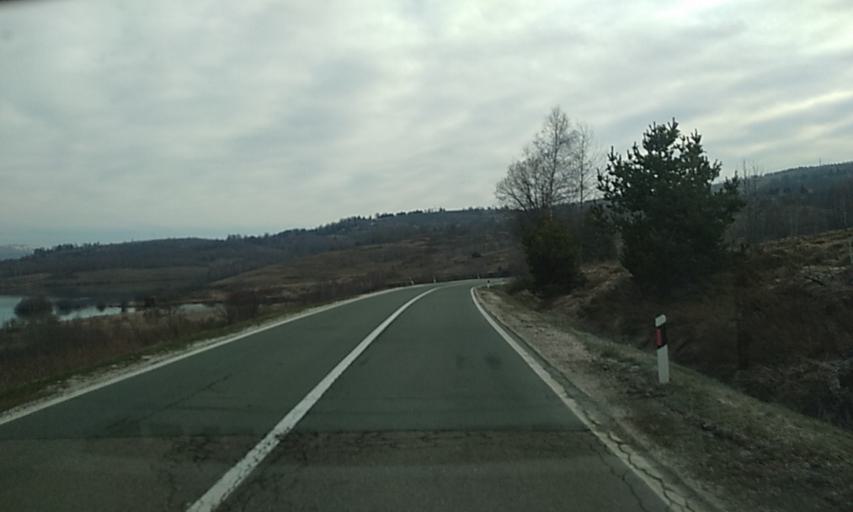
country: RS
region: Central Serbia
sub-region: Jablanicki Okrug
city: Crna Trava
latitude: 42.6765
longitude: 22.3502
